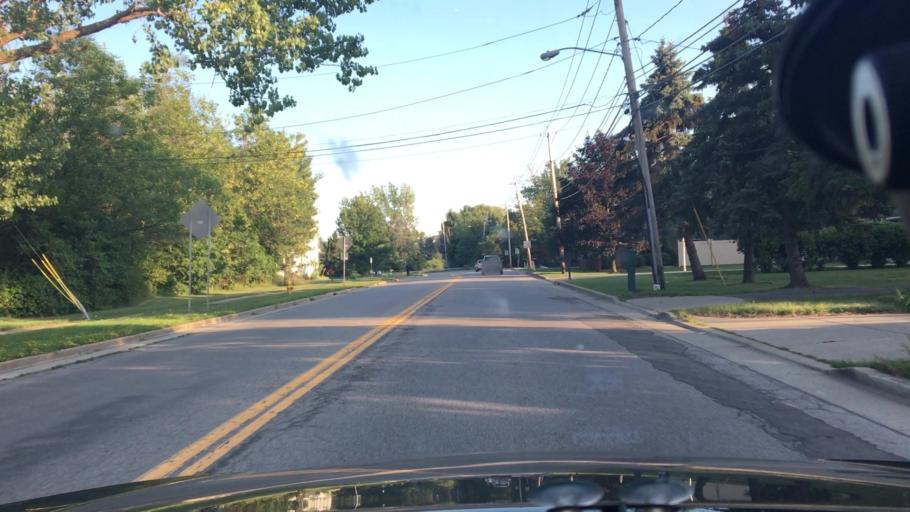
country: US
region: New York
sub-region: Erie County
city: Amherst
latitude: 43.0055
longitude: -78.7634
